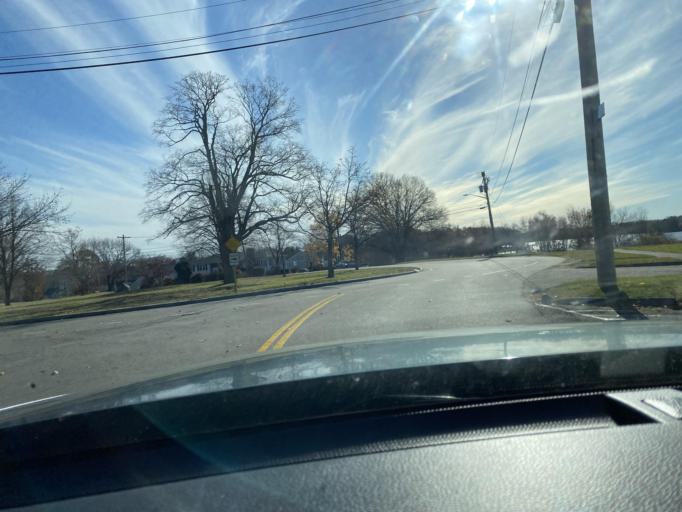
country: US
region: Massachusetts
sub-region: Norfolk County
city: Westwood
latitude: 42.1841
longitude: -71.2337
